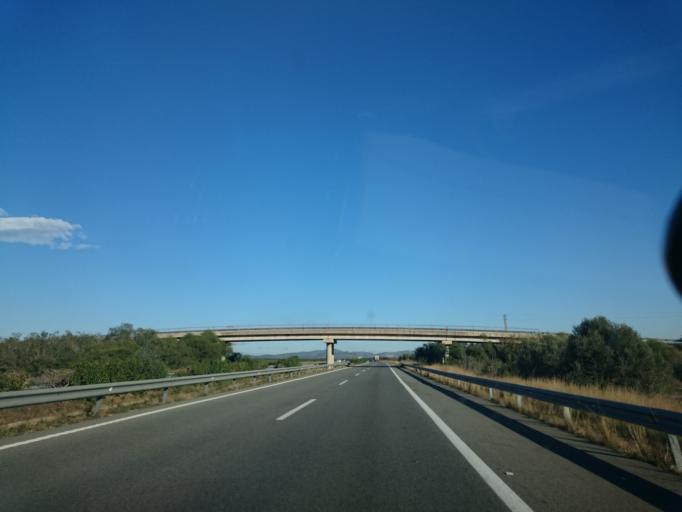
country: ES
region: Catalonia
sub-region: Provincia de Tarragona
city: Alcanar
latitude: 40.5242
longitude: 0.4171
